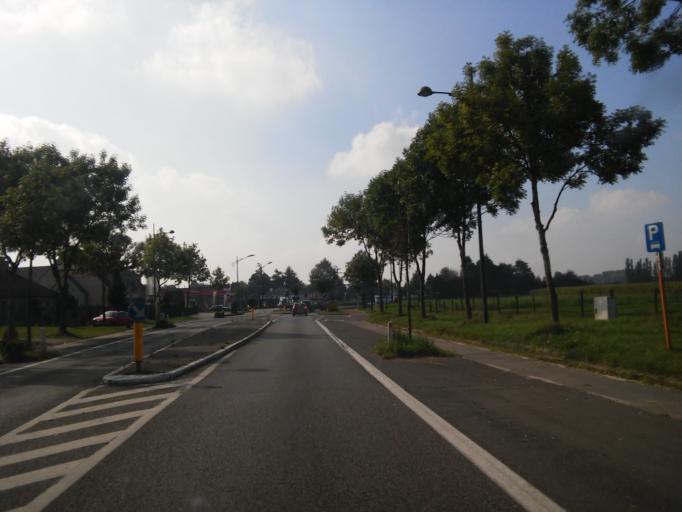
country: BE
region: Flanders
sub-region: Provincie Oost-Vlaanderen
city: Berlare
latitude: 51.0514
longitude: 3.9757
